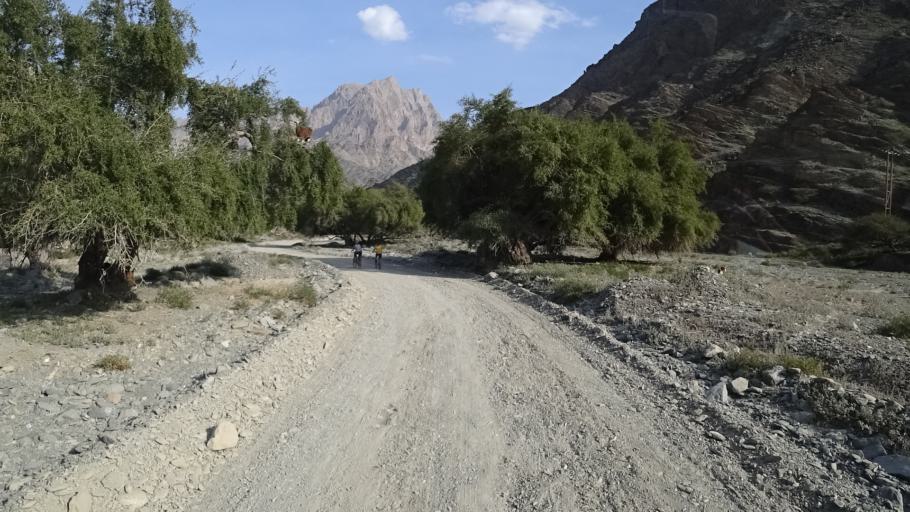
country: OM
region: Al Batinah
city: Bayt al `Awabi
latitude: 23.2567
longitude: 57.4196
